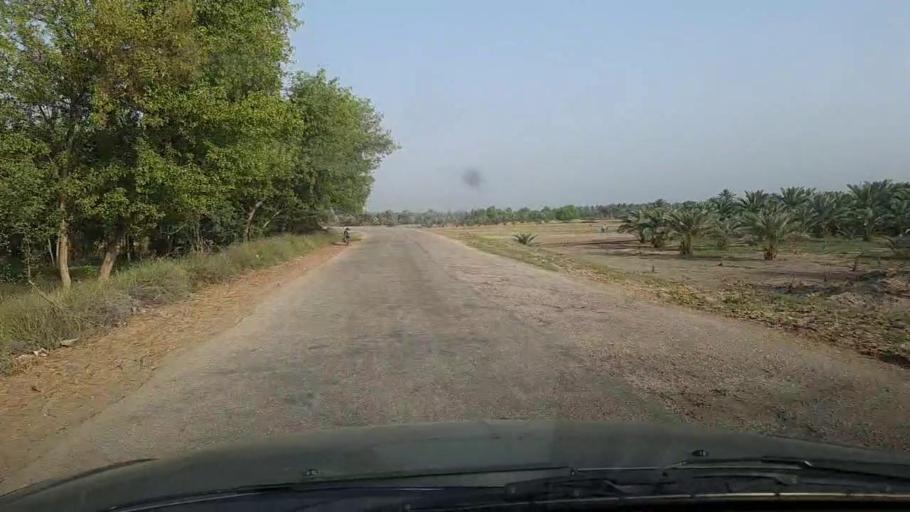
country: PK
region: Sindh
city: Pir jo Goth
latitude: 27.5625
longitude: 68.6588
